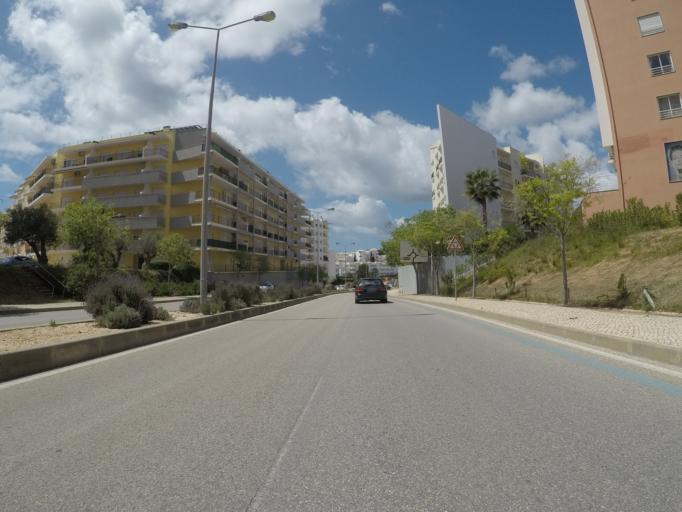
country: PT
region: Faro
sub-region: Silves
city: Armacao de Pera
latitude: 37.1045
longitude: -8.3683
